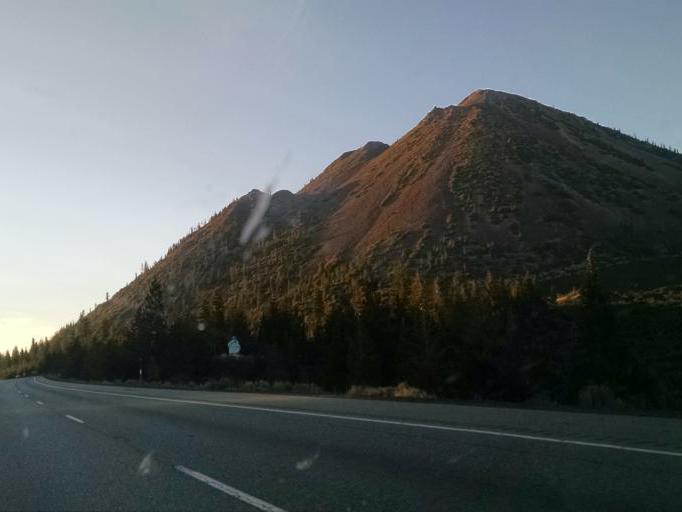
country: US
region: California
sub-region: Siskiyou County
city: Mount Shasta
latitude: 41.3487
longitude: -122.3480
